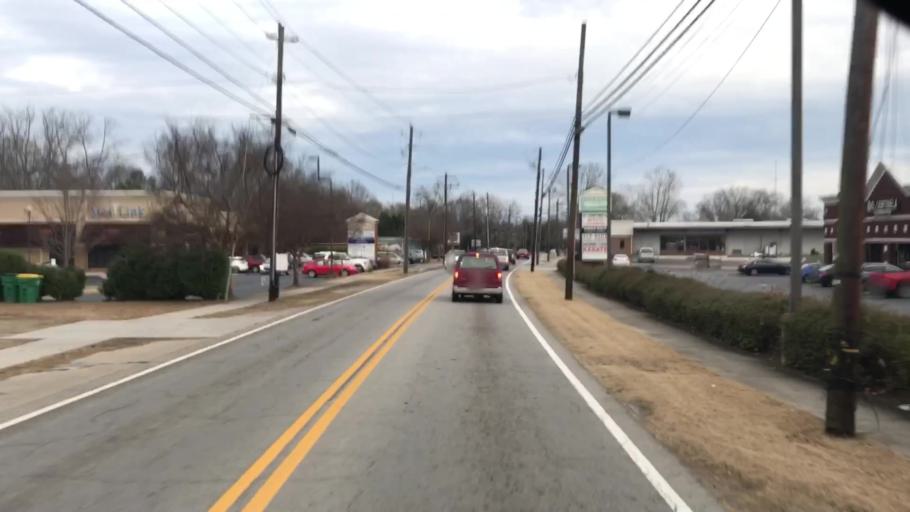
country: US
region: Georgia
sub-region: Barrow County
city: Winder
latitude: 33.9949
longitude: -83.7276
